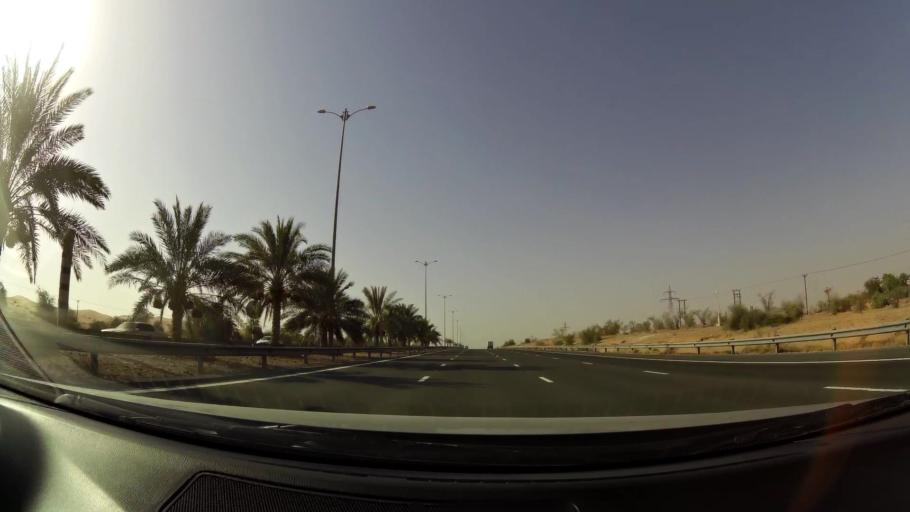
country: OM
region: Al Buraimi
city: Al Buraymi
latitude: 24.6211
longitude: 55.7252
